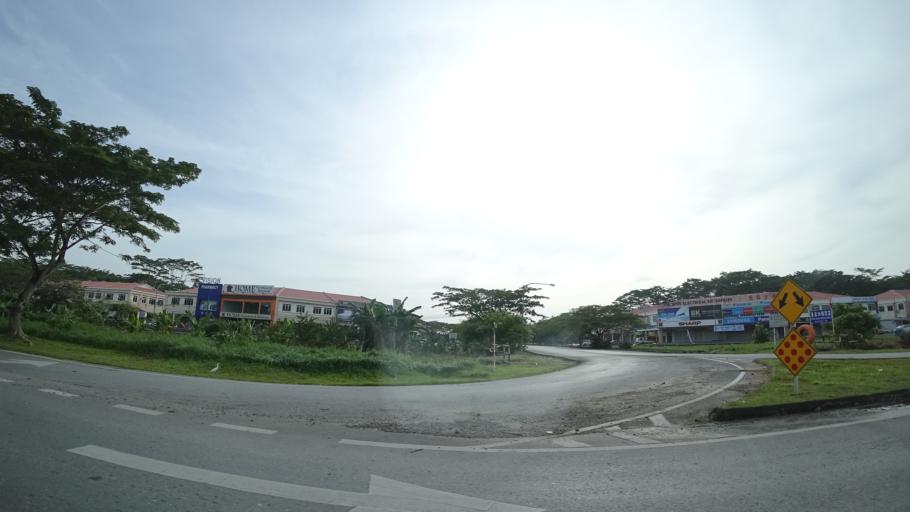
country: MY
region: Sarawak
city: Miri
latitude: 4.4749
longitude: 114.0420
